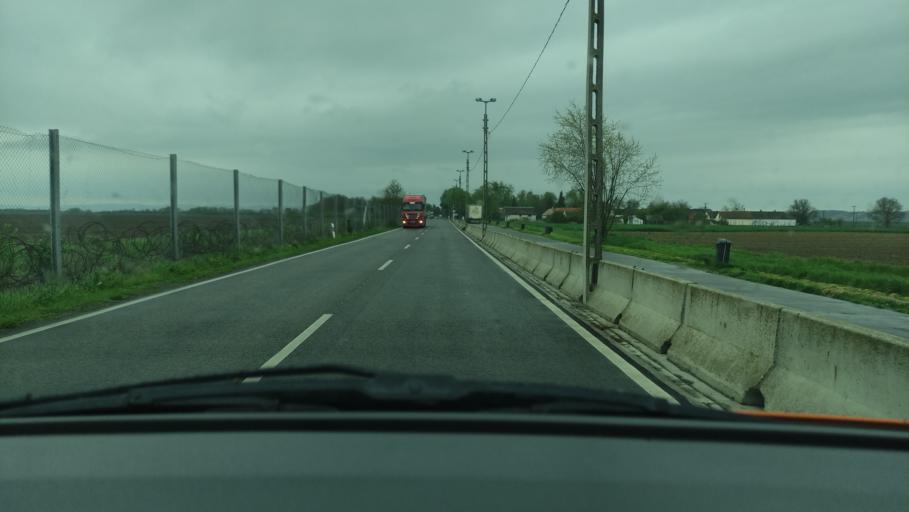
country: HU
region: Baranya
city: Mohacs
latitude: 45.9073
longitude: 18.6596
